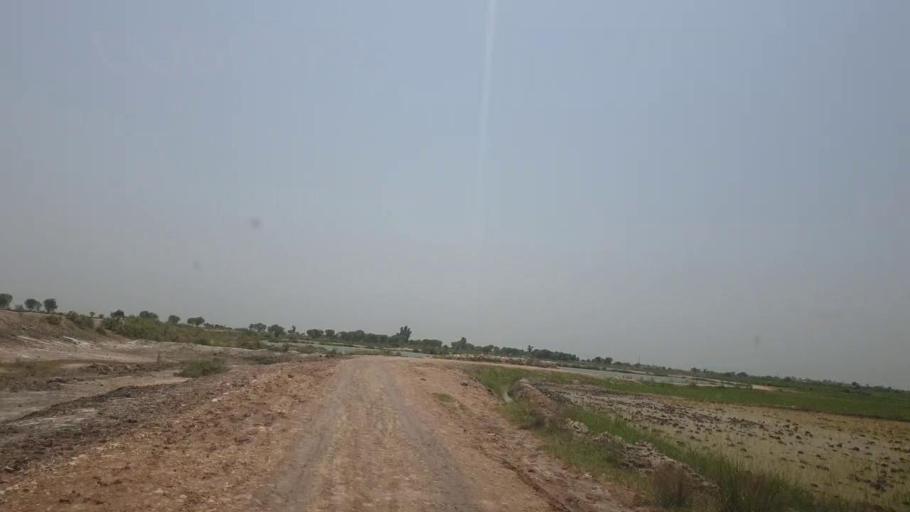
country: PK
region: Sindh
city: Lakhi
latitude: 27.8538
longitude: 68.6652
